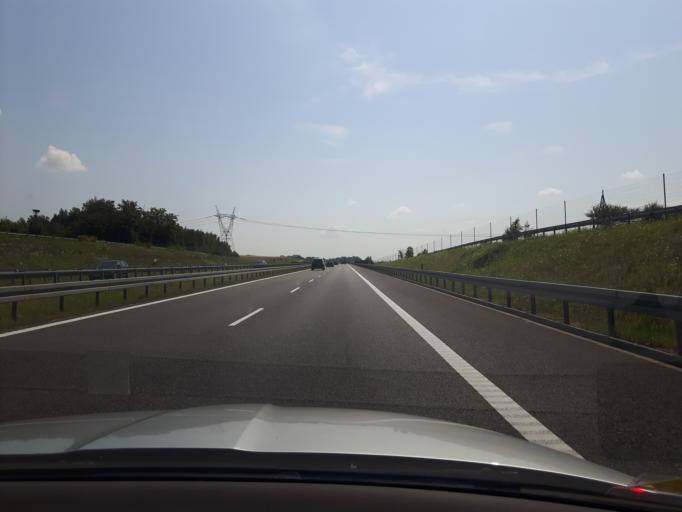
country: PL
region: Warmian-Masurian Voivodeship
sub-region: Powiat elblaski
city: Gronowo Gorne
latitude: 54.1220
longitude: 19.4666
